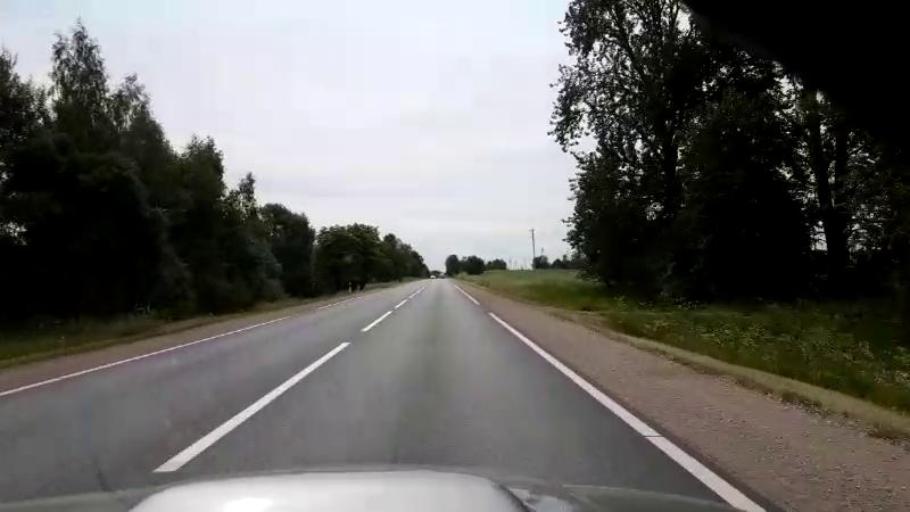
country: LV
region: Bauskas Rajons
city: Bauska
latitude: 56.4951
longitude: 24.1757
